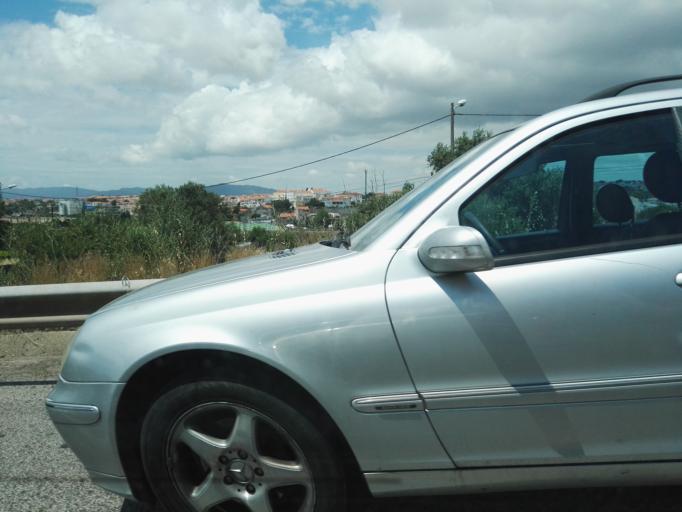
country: PT
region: Lisbon
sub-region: Oeiras
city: Terrugem
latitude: 38.7111
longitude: -9.2904
